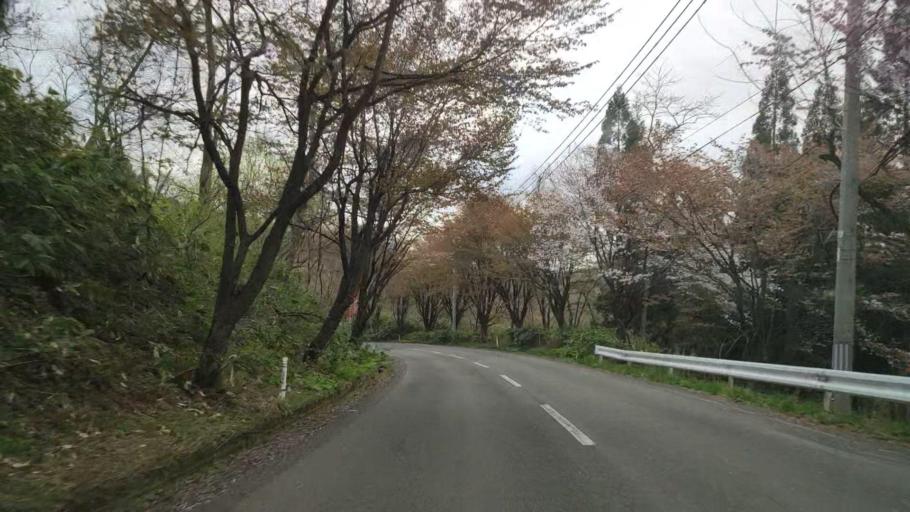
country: JP
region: Akita
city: Hanawa
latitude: 40.3614
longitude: 140.7858
